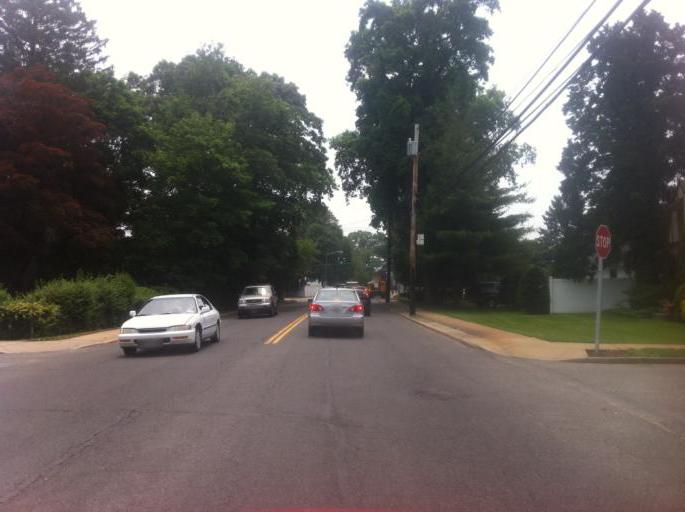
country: US
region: New York
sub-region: Nassau County
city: Massapequa
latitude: 40.6864
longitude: -73.4765
